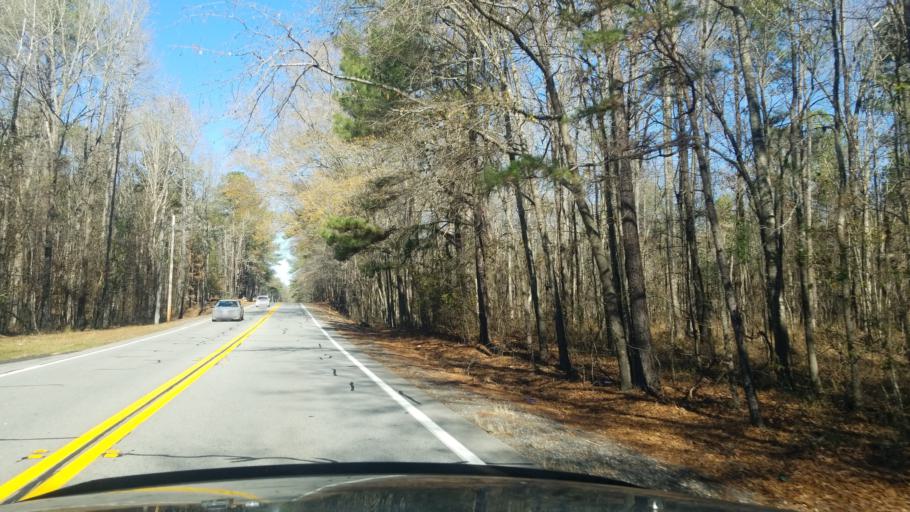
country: US
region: Georgia
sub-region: Harris County
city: Hamilton
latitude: 32.6673
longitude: -84.8587
